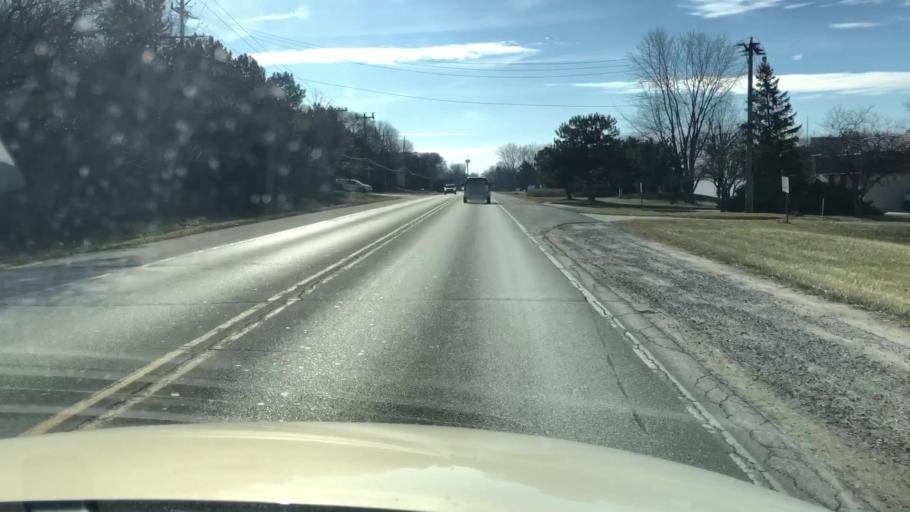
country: US
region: Wisconsin
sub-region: Waukesha County
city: Brookfield
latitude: 43.0521
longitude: -88.1666
